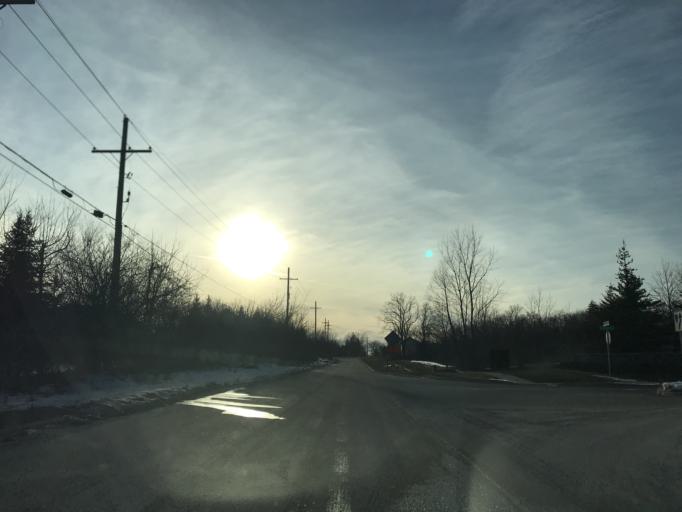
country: US
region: Michigan
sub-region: Wayne County
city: Northville
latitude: 42.4495
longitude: -83.5497
